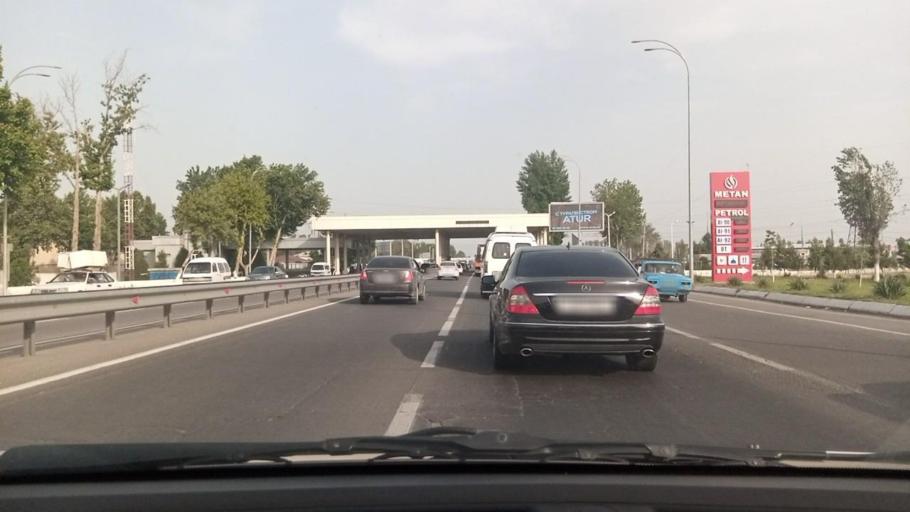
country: UZ
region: Toshkent Shahri
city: Bektemir
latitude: 41.2487
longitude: 69.3908
